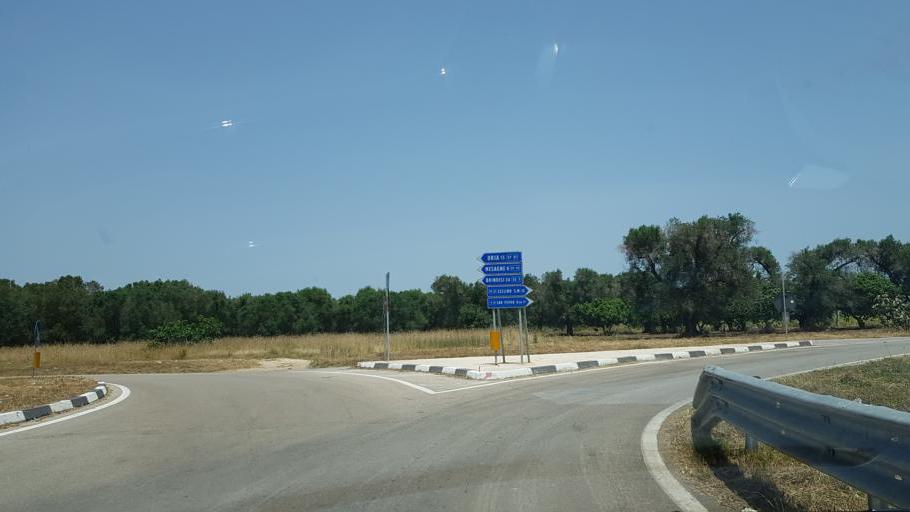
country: IT
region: Apulia
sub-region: Provincia di Brindisi
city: San Pancrazio Salentino
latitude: 40.4855
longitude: 17.8343
